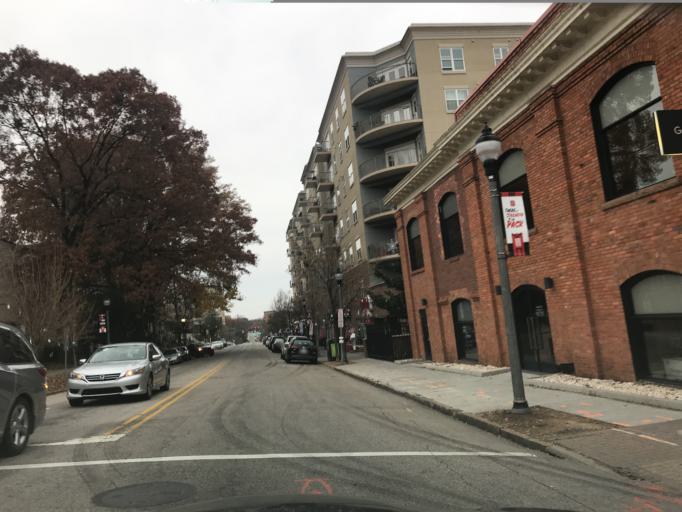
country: US
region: North Carolina
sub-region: Wake County
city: Raleigh
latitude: 35.7828
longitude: -78.6475
